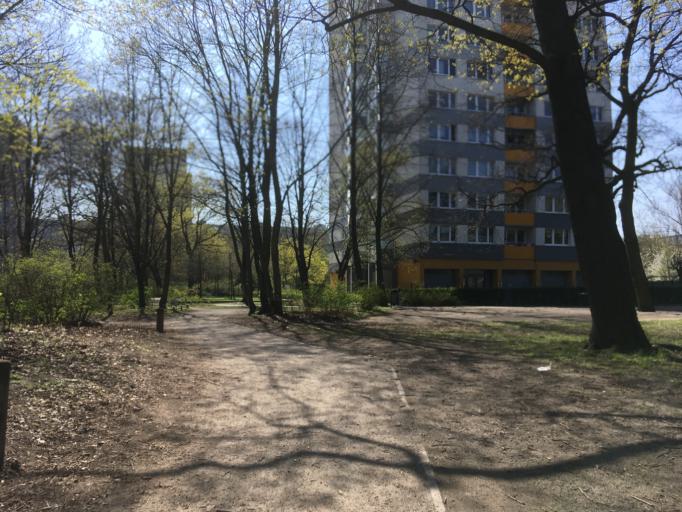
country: DE
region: Berlin
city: Friedrichsfelde
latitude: 52.4969
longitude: 13.5165
